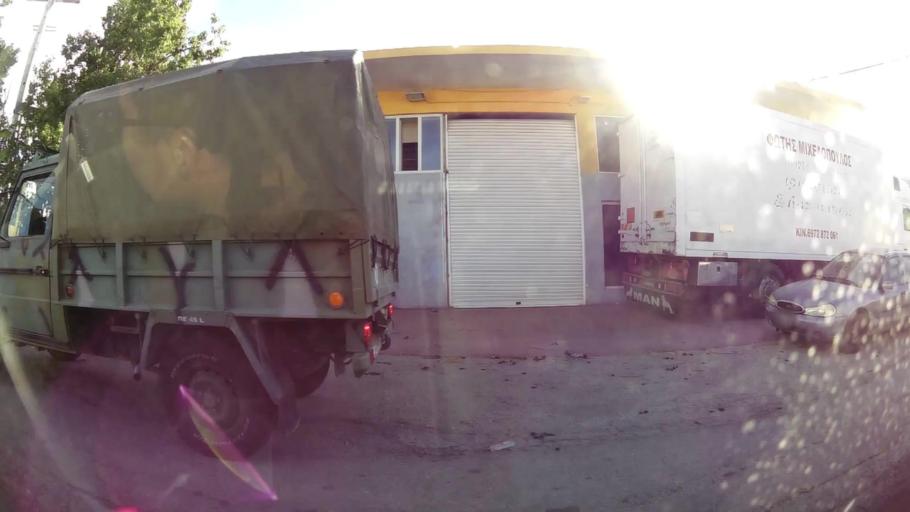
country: GR
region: Attica
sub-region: Nomarchia Anatolikis Attikis
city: Acharnes
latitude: 38.0684
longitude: 23.7390
